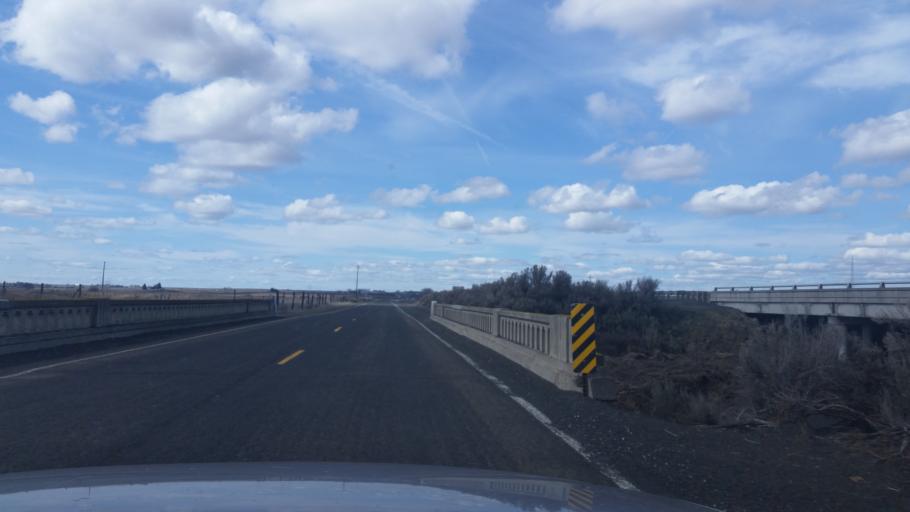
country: US
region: Washington
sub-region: Grant County
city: Warden
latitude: 47.0848
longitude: -119.0161
